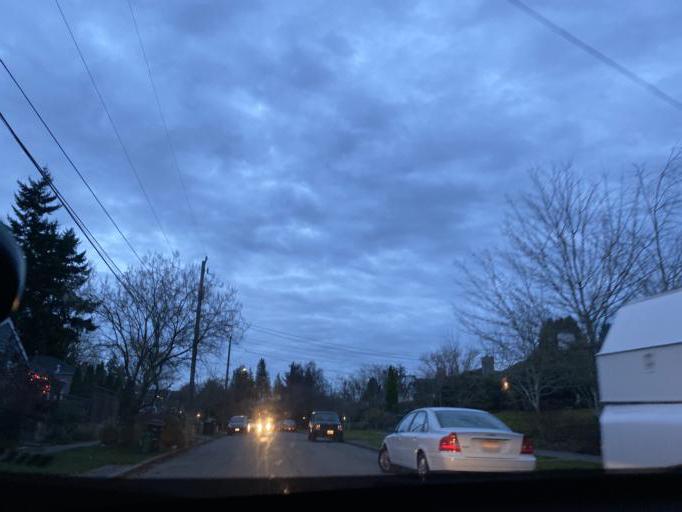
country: US
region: Washington
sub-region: King County
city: Seattle
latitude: 47.6552
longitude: -122.3945
